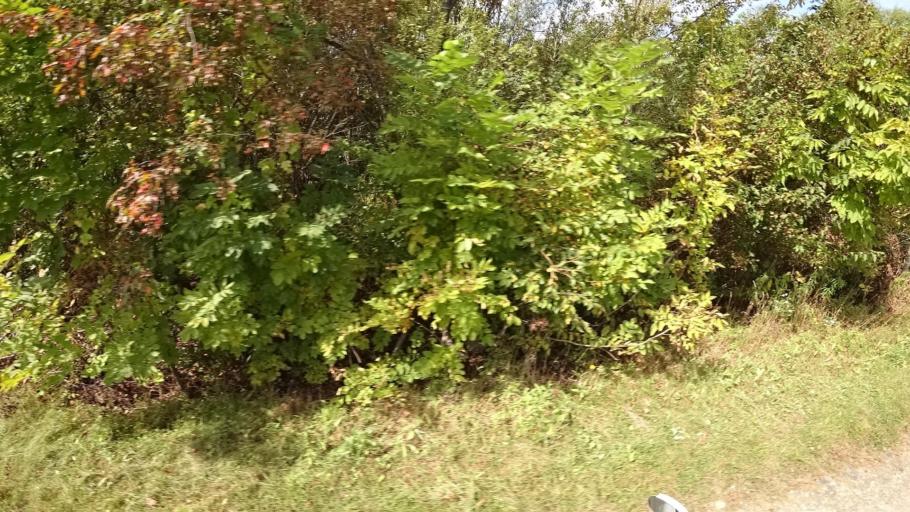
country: RU
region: Primorskiy
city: Yakovlevka
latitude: 44.7094
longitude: 133.6291
